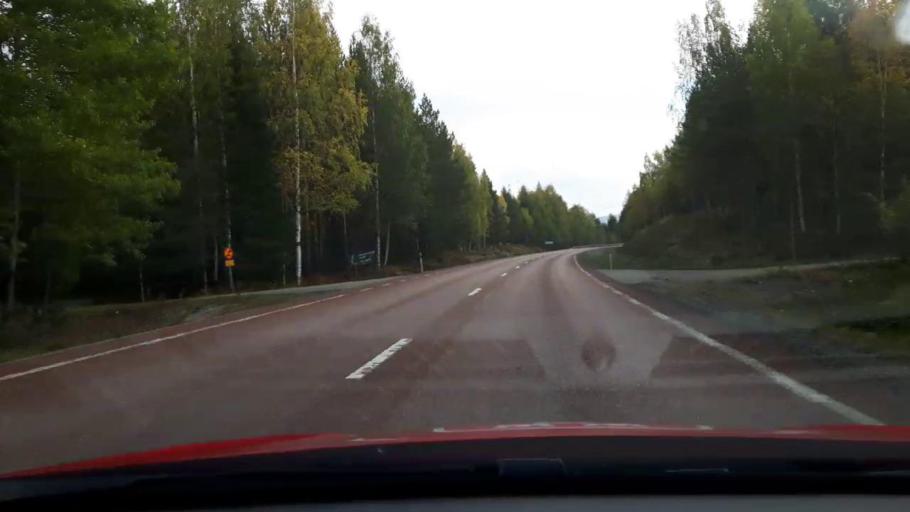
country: SE
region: Gaevleborg
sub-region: Ljusdals Kommun
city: Jaervsoe
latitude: 61.6360
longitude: 16.2619
